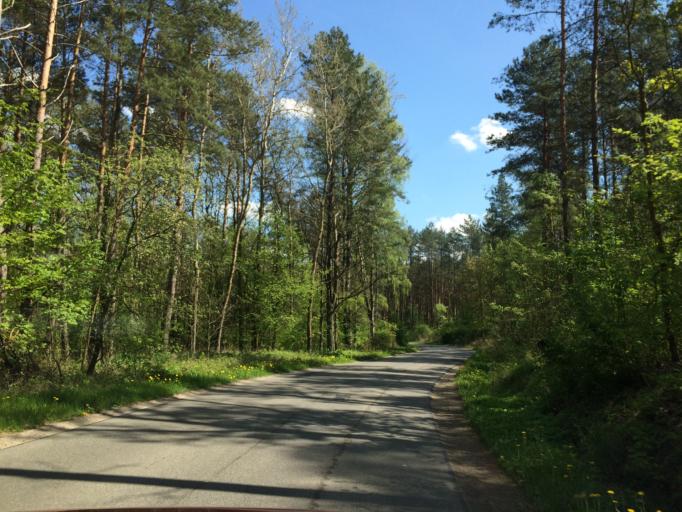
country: PL
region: Warmian-Masurian Voivodeship
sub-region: Powiat ilawski
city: Lubawa
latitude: 53.3888
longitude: 19.7242
